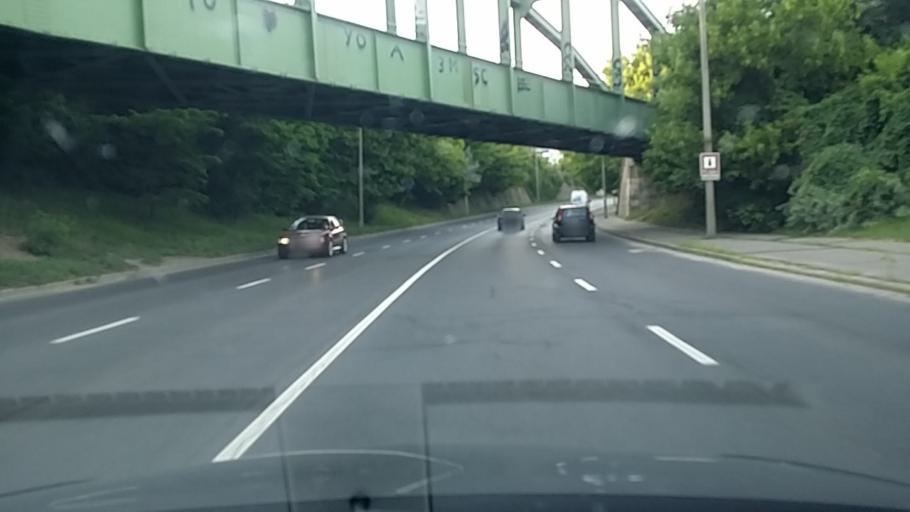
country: HU
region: Borsod-Abauj-Zemplen
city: Miskolc
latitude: 48.0777
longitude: 20.7845
